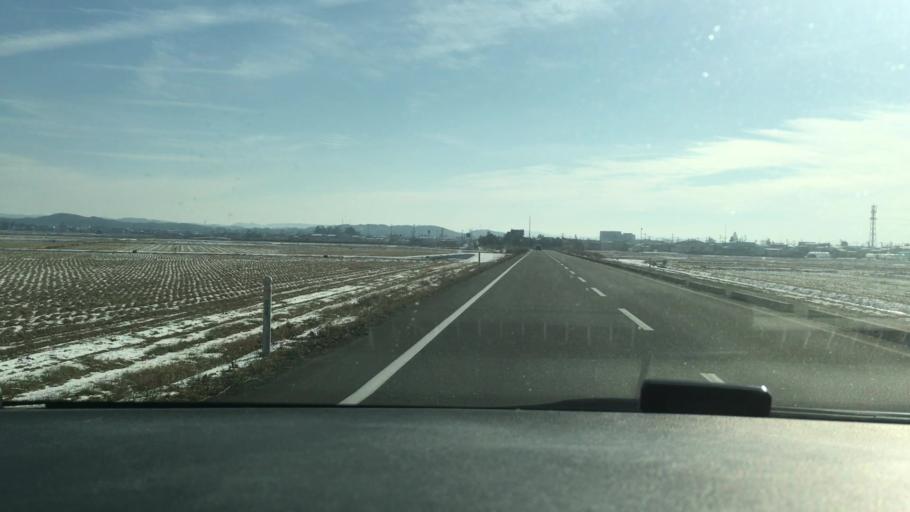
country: JP
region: Iwate
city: Ichinoseki
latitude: 38.7801
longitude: 141.1264
